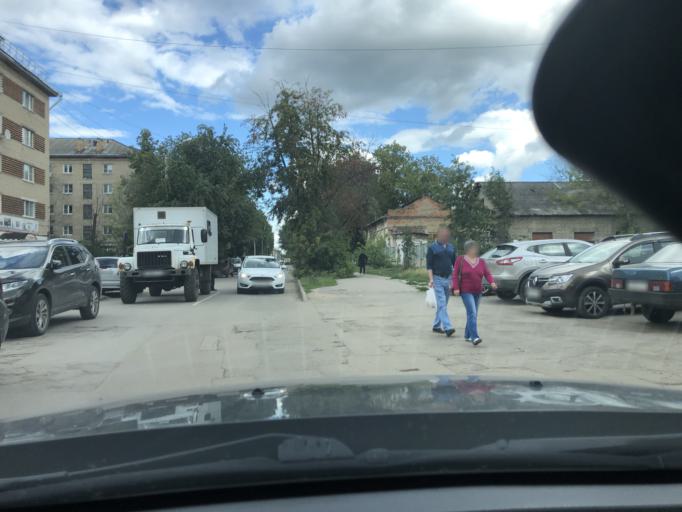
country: RU
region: Tula
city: Novomoskovsk
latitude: 54.0144
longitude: 38.2803
